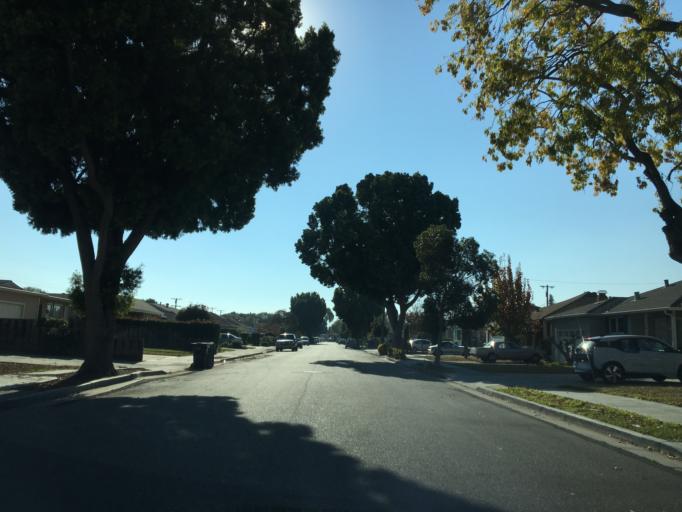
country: US
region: California
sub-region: Santa Clara County
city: Sunnyvale
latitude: 37.4021
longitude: -122.0222
